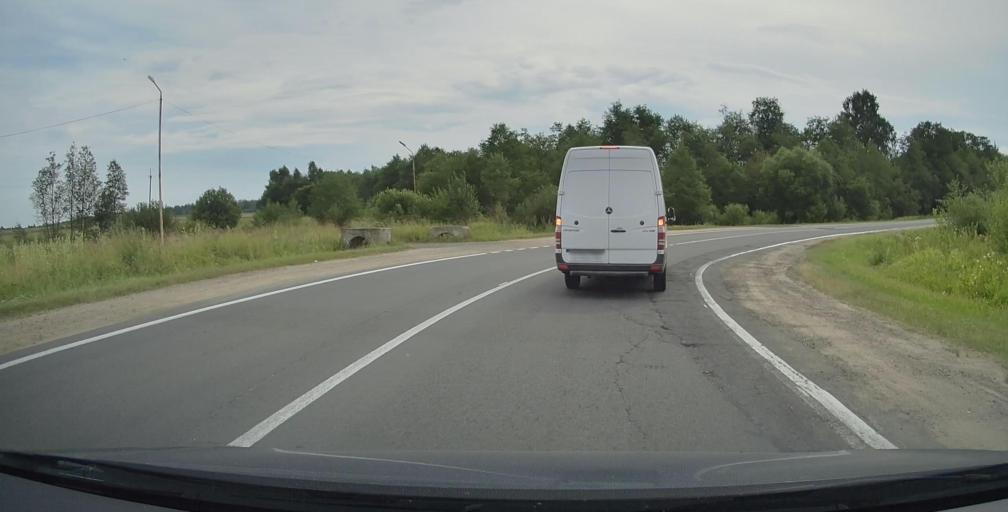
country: RU
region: Jaroslavl
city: Rybinsk
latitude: 57.9779
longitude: 38.7478
